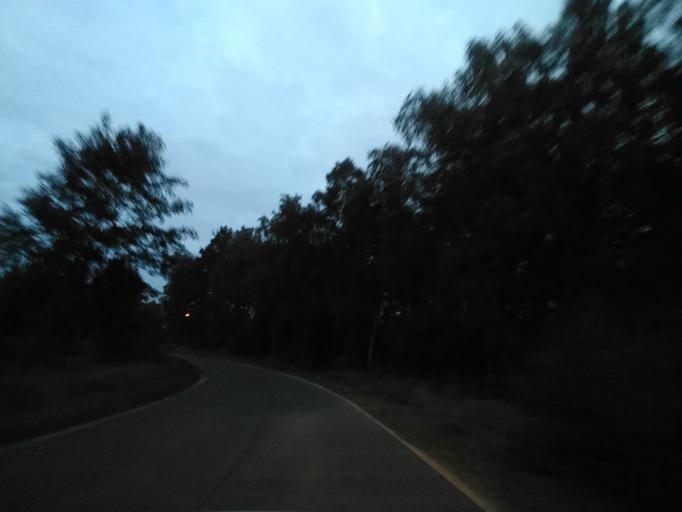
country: PL
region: Kujawsko-Pomorskie
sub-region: Powiat golubsko-dobrzynski
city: Kowalewo Pomorskie
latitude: 53.1405
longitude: 18.9671
